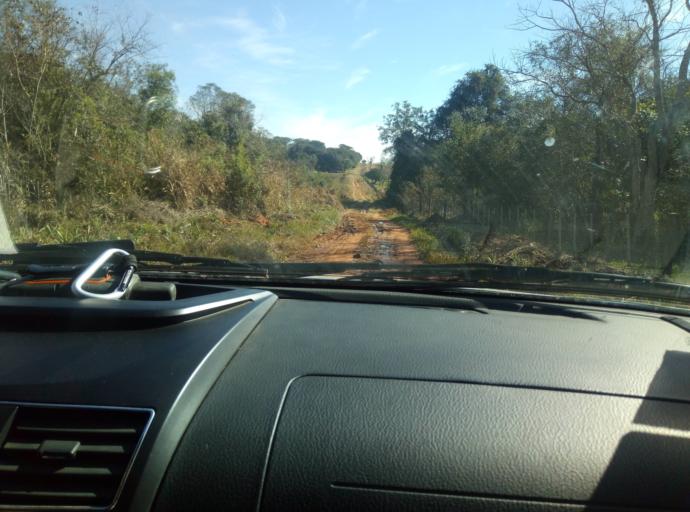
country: PY
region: Caaguazu
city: Carayao
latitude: -25.1752
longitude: -56.3102
